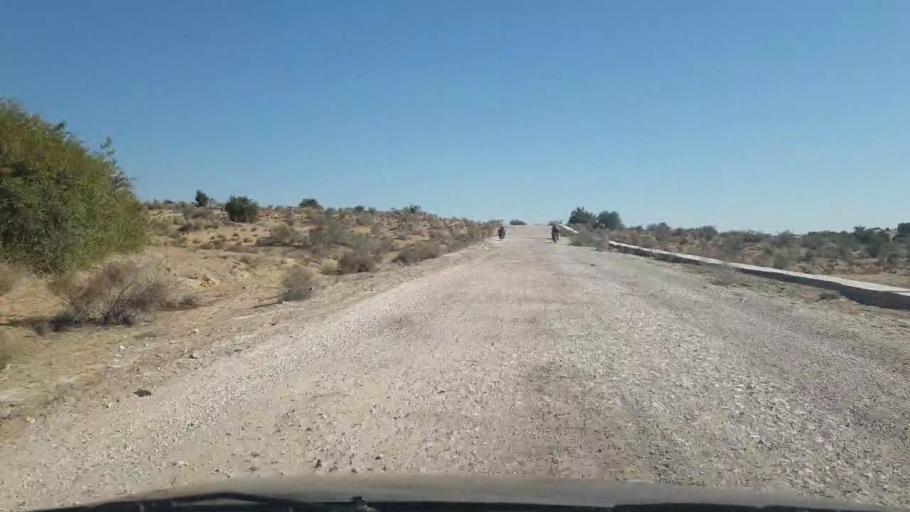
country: PK
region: Sindh
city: Bozdar
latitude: 27.0036
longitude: 68.8822
